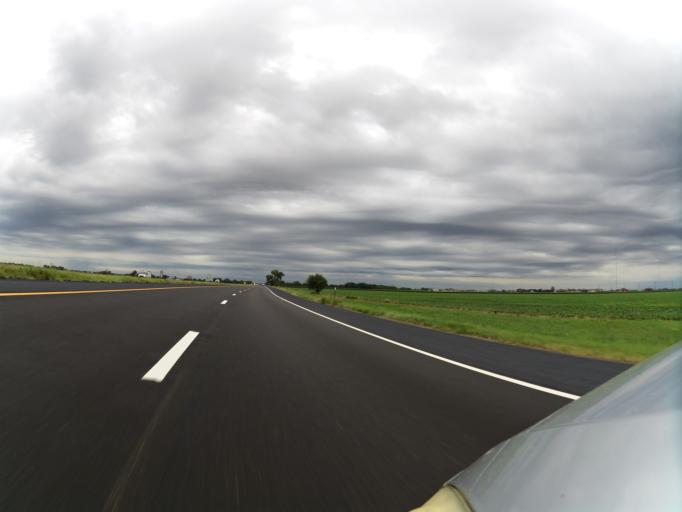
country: US
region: Kansas
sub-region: Sedgwick County
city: Colwich
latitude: 37.8220
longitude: -97.5126
